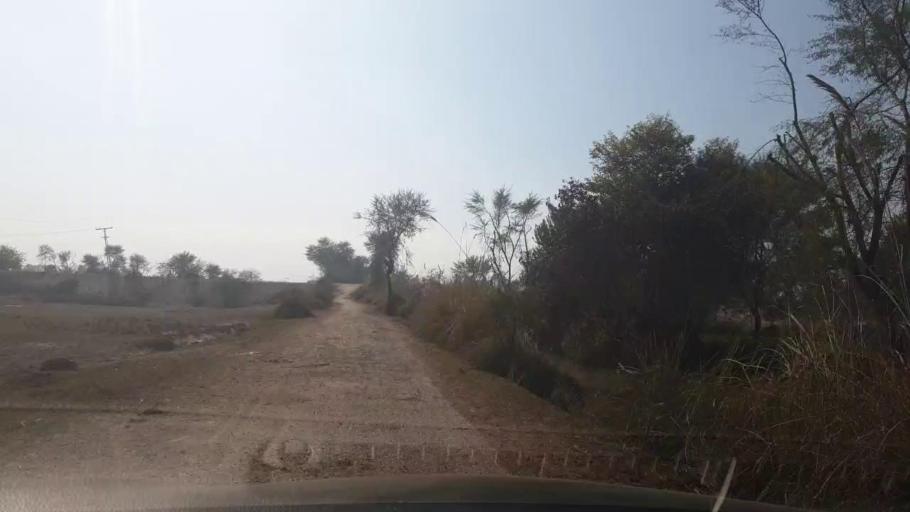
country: PK
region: Sindh
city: Ubauro
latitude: 28.1376
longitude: 69.6833
